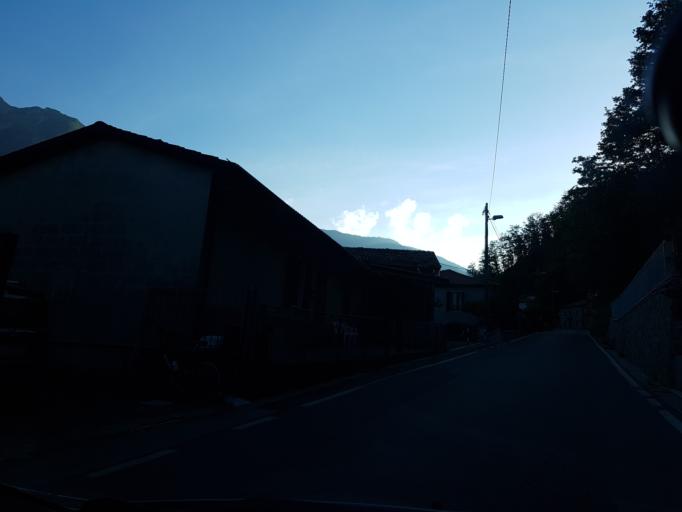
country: IT
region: Tuscany
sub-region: Provincia di Lucca
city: Minucciano
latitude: 44.1621
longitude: 10.2314
